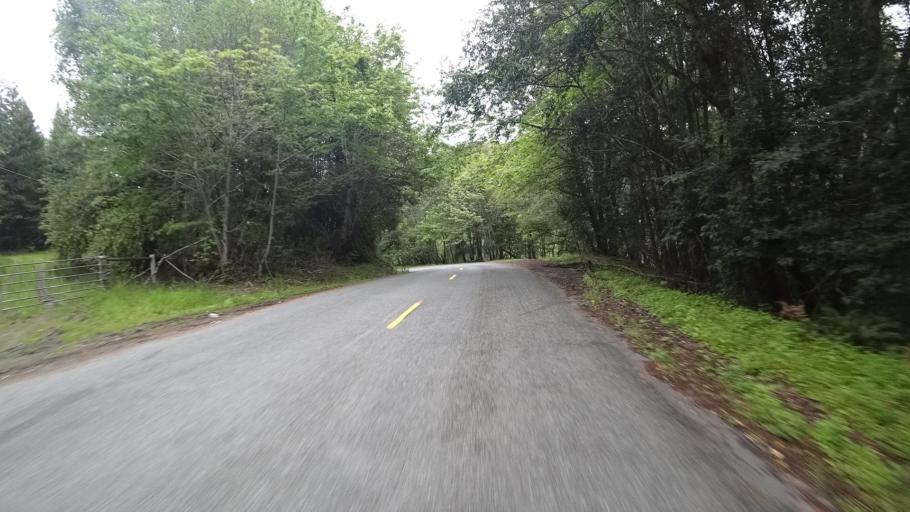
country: US
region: California
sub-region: Humboldt County
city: Blue Lake
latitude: 40.9491
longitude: -123.8406
